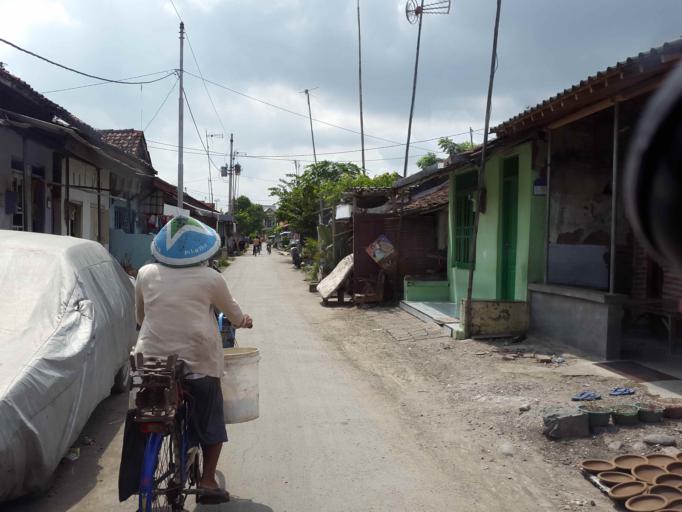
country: ID
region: Central Java
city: Pemalang
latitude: -6.8855
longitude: 109.3846
